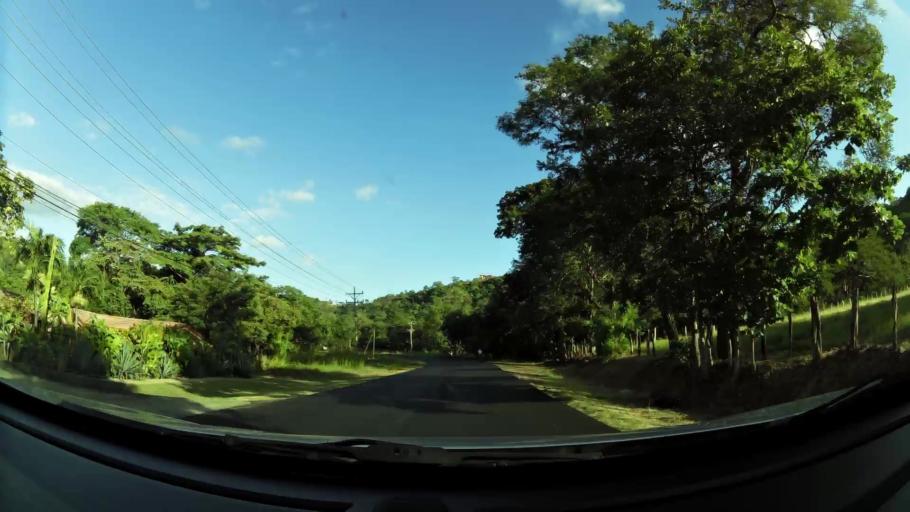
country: CR
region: Guanacaste
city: Sardinal
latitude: 10.5358
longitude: -85.6828
